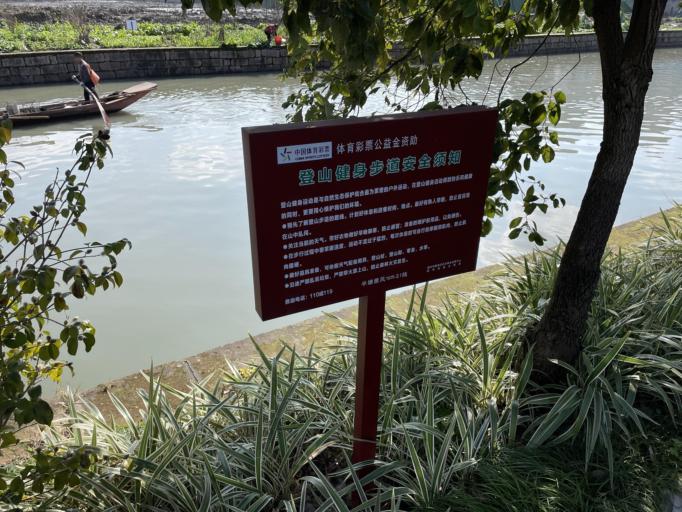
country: CN
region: Zhejiang Sheng
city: Louqiao
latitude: 27.9805
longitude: 120.6191
